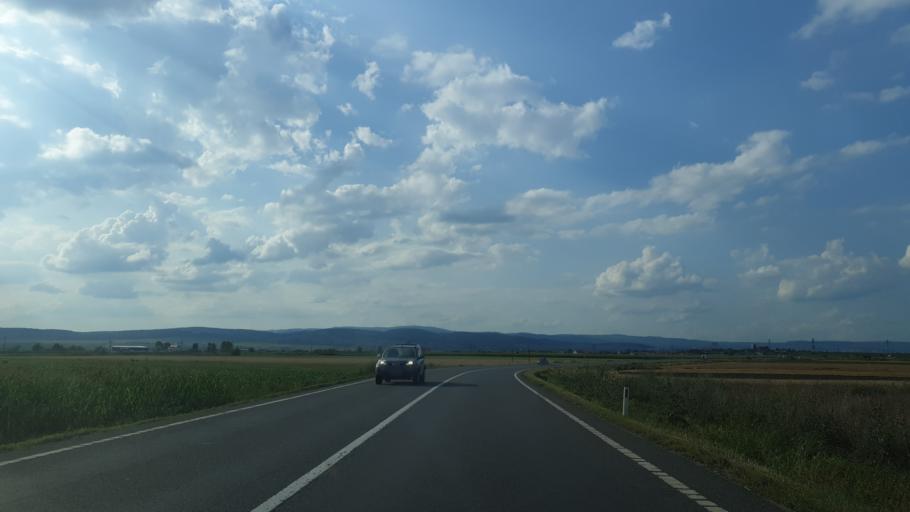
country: RO
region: Covasna
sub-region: Comuna Chichis
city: Chichis
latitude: 45.7931
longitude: 25.8054
